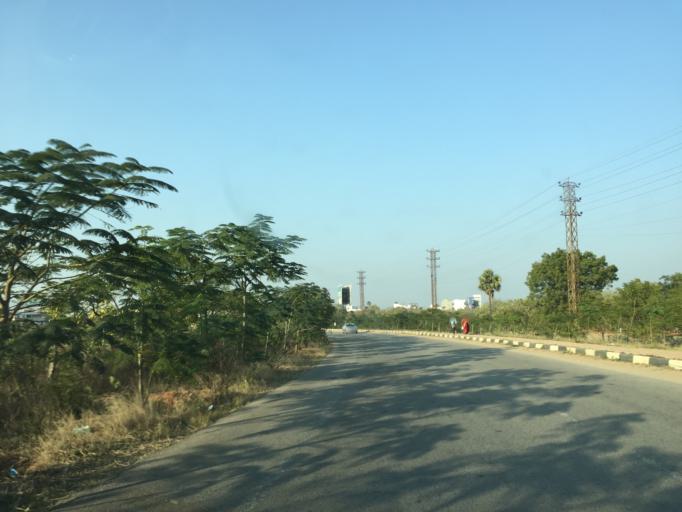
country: IN
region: Telangana
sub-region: Rangareddi
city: Ghatkesar
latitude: 17.4401
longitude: 78.6728
